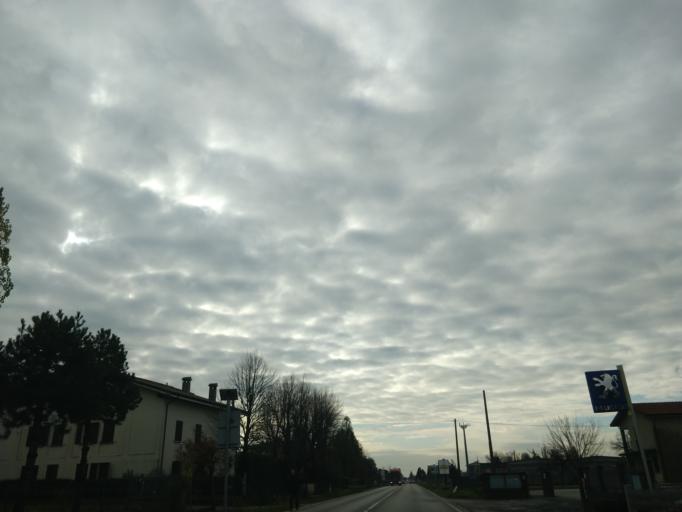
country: IT
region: Emilia-Romagna
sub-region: Provincia di Bologna
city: Pieve di Cento
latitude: 44.7079
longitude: 11.3058
